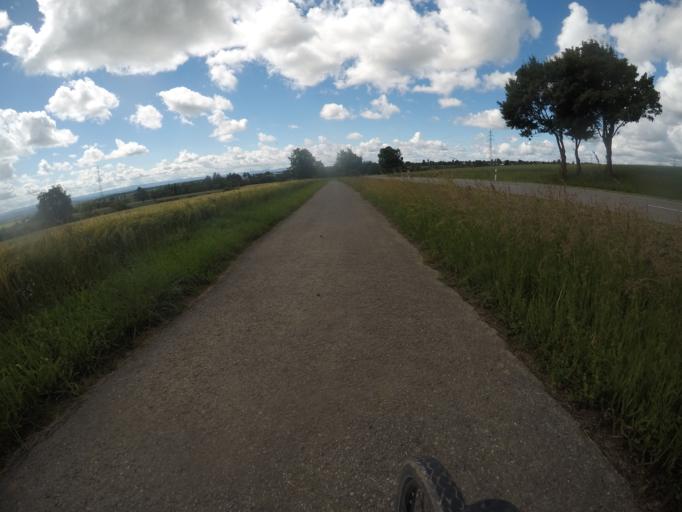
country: DE
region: Baden-Wuerttemberg
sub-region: Regierungsbezirk Stuttgart
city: Motzingen
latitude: 48.5434
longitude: 8.7783
